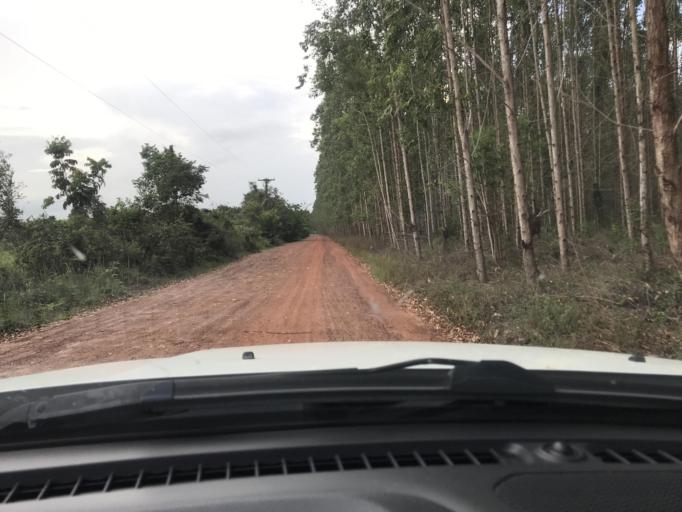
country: BR
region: Bahia
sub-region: Entre Rios
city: Entre Rios
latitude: -12.1165
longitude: -38.1797
